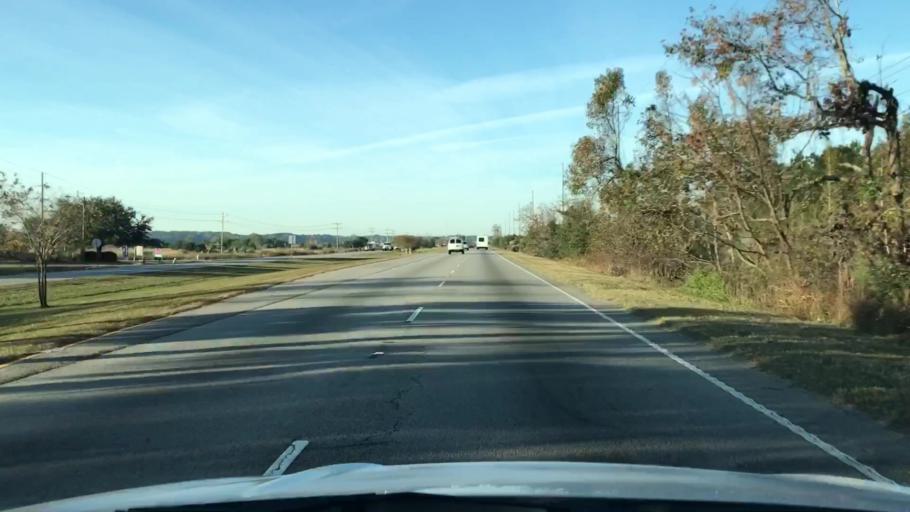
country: US
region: South Carolina
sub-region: Charleston County
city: Shell Point
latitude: 32.7998
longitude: -80.1282
